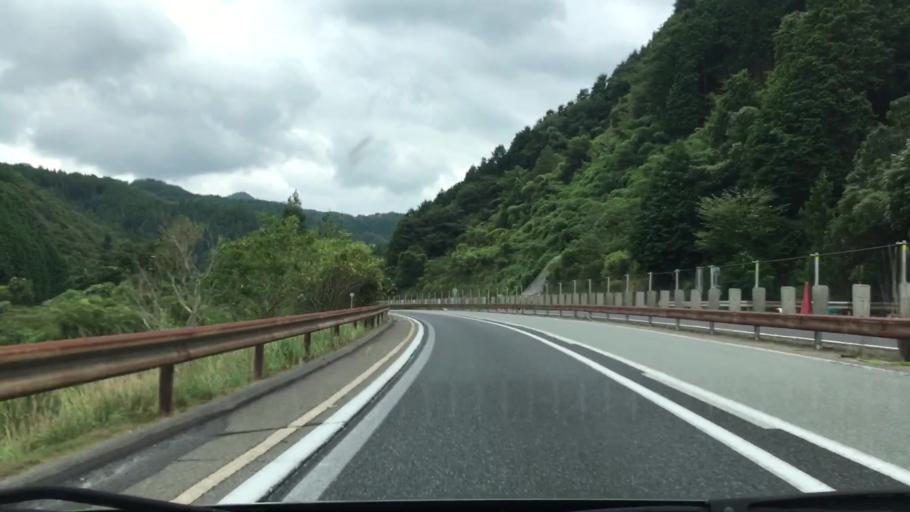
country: JP
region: Okayama
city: Niimi
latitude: 35.0228
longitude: 133.5237
